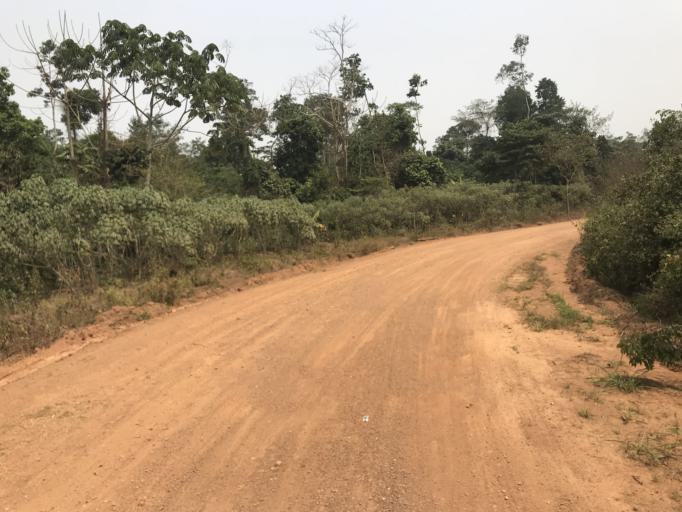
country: NG
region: Osun
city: Ifetedo
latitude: 7.0385
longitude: 4.4572
